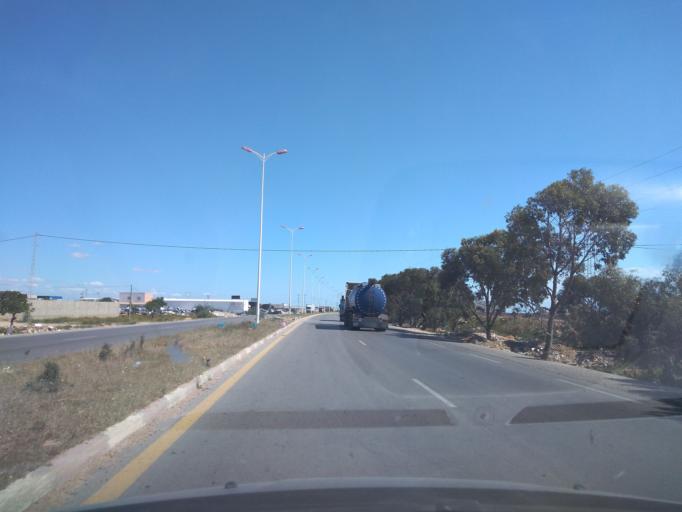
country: TN
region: Safaqis
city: Sfax
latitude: 34.8160
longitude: 10.7002
